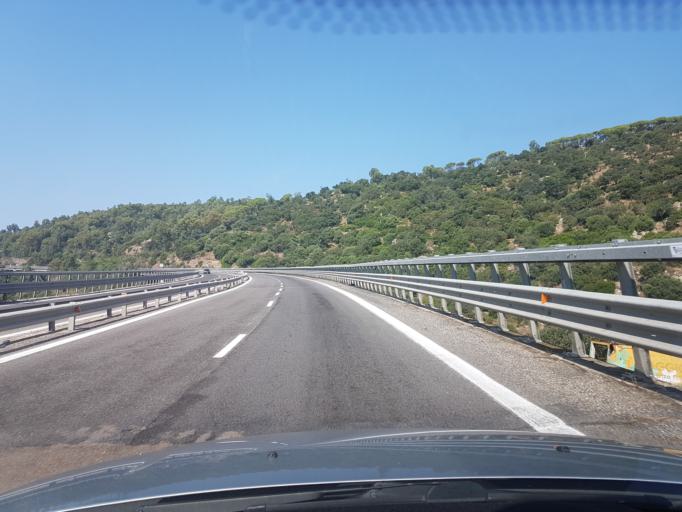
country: IT
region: Sardinia
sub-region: Provincia di Nuoro
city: Nuoro
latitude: 40.3399
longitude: 9.3060
